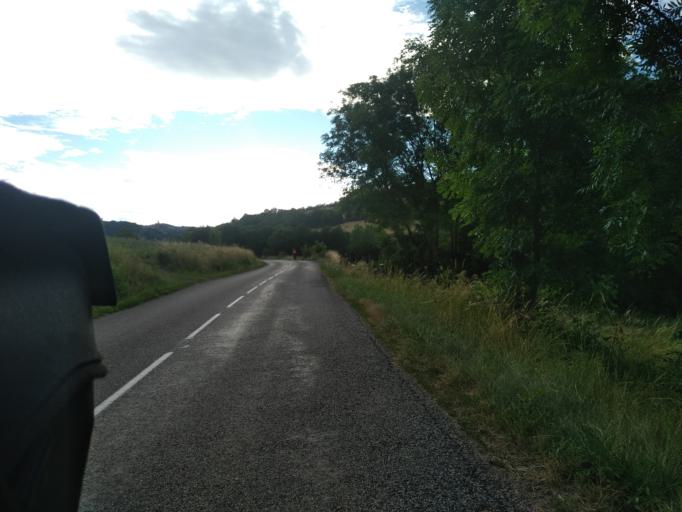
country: FR
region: Rhone-Alpes
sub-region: Departement du Rhone
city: Montrottier
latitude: 45.7890
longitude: 4.5096
